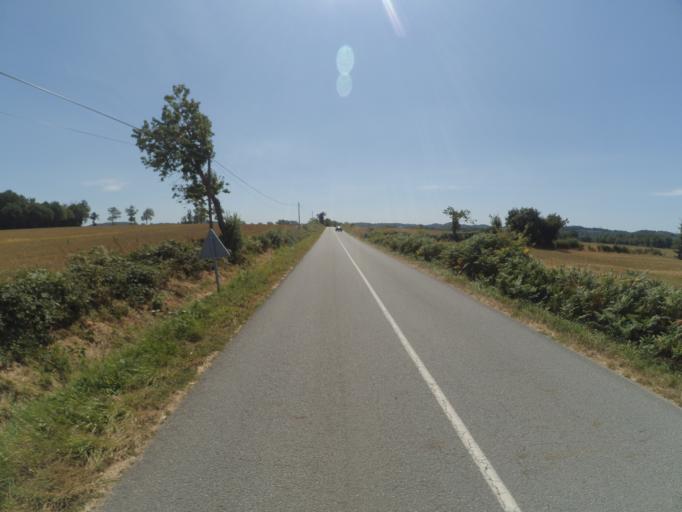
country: FR
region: Limousin
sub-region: Departement de la Creuse
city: Le Grand-Bourg
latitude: 46.1978
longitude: 1.6127
